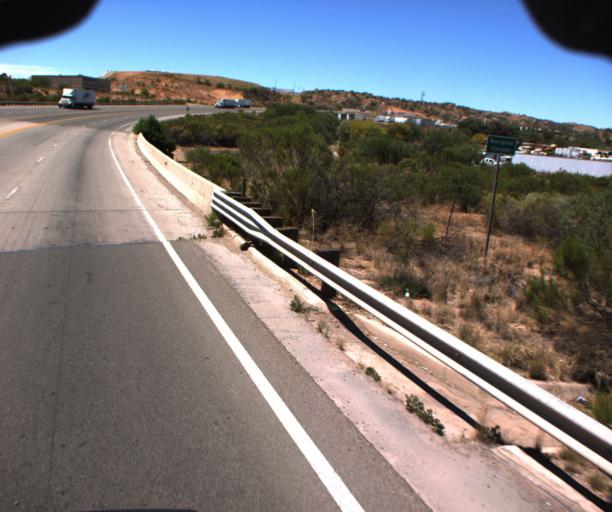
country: US
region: Arizona
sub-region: Santa Cruz County
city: Nogales
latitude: 31.3537
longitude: -110.9600
